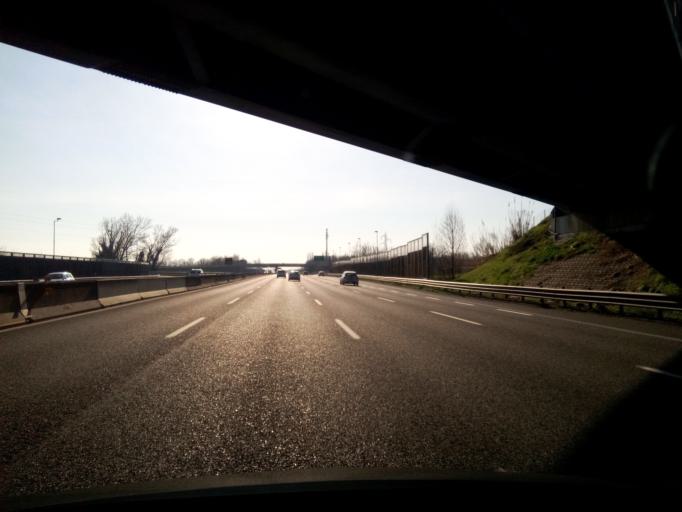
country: IT
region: Emilia-Romagna
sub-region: Provincia di Modena
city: San Vito
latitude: 44.5796
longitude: 10.9781
